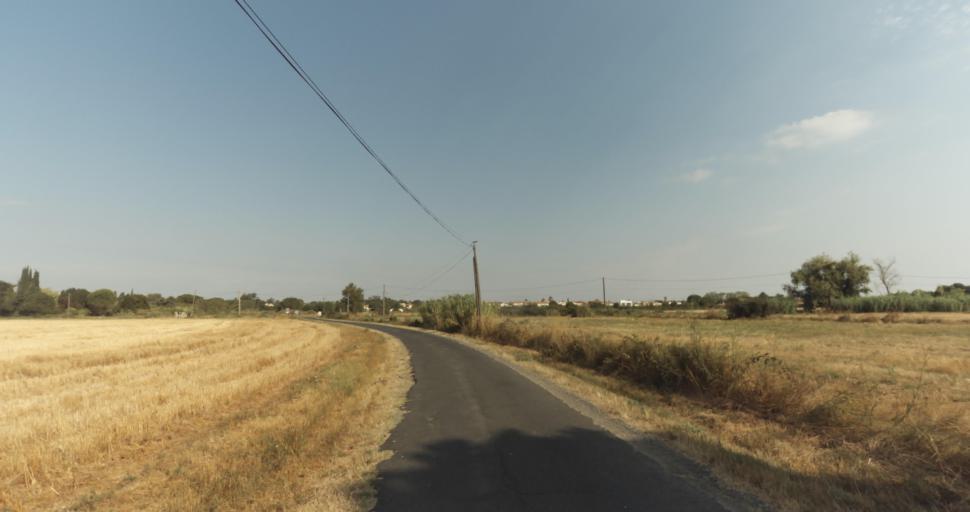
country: FR
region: Languedoc-Roussillon
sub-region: Departement des Pyrenees-Orientales
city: Latour-Bas-Elne
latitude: 42.6110
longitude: 3.0184
